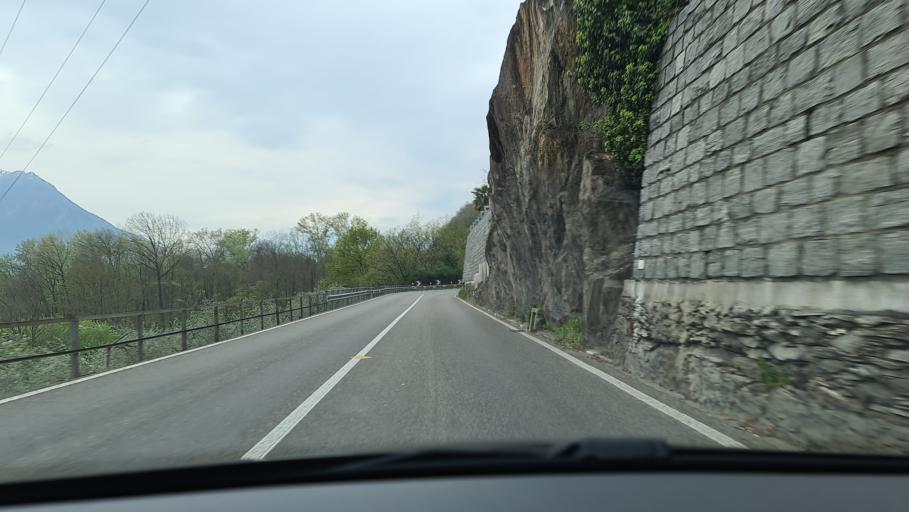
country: CH
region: Ticino
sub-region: Bellinzona District
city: Sementina
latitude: 46.1768
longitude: 8.9667
